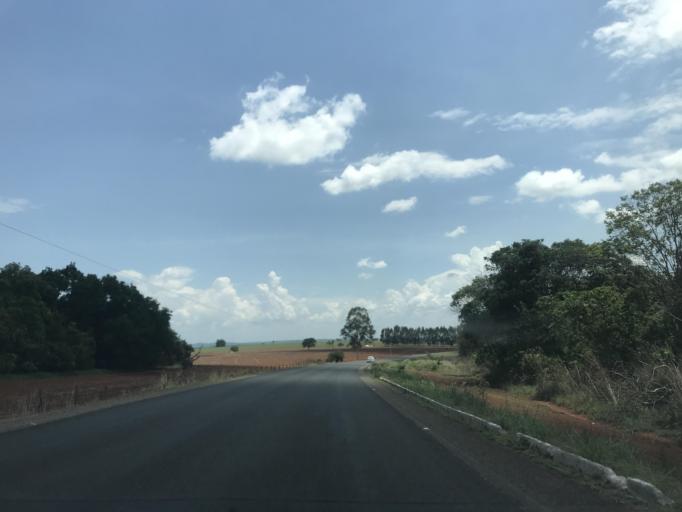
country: BR
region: Goias
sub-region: Bela Vista De Goias
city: Bela Vista de Goias
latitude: -17.0909
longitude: -48.6533
